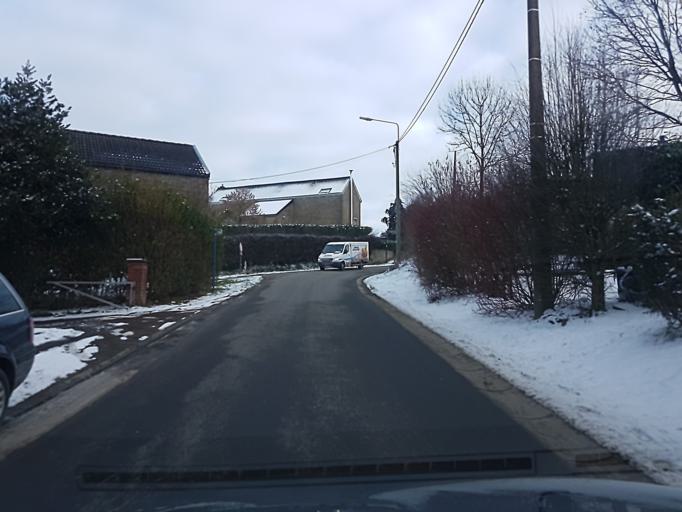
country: BE
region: Wallonia
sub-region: Province de Liege
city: Pepinster
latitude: 50.5848
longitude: 5.7872
